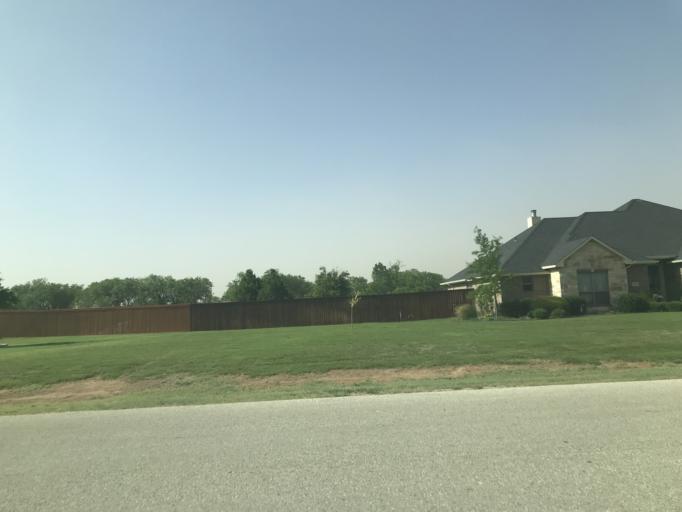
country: US
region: Texas
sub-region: Taylor County
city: Potosi
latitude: 32.3507
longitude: -99.7091
